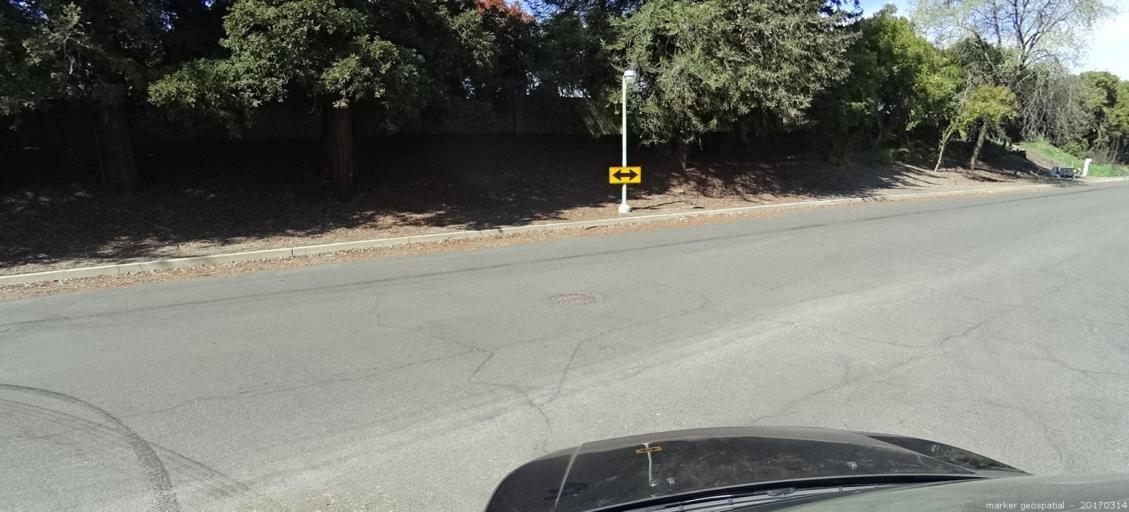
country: US
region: California
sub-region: Yolo County
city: West Sacramento
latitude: 38.5196
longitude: -121.5212
